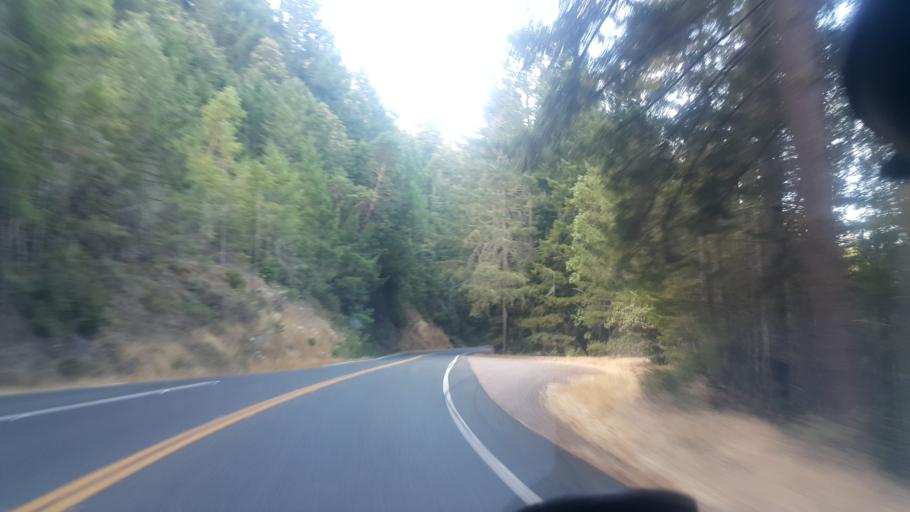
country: US
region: California
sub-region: Mendocino County
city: Brooktrails
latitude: 39.3835
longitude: -123.4740
